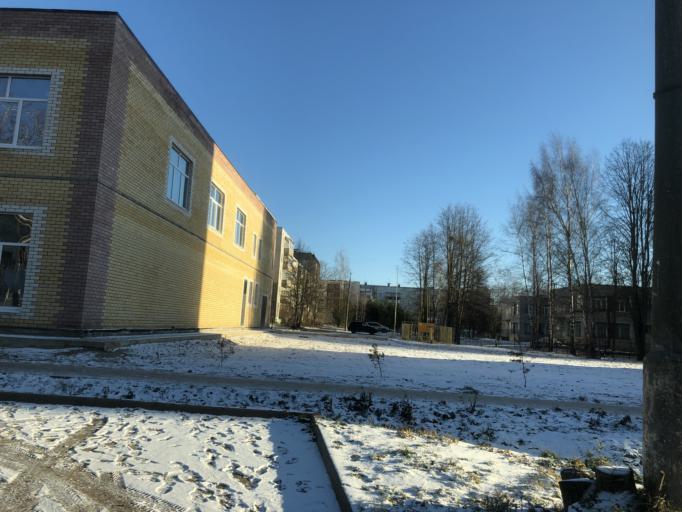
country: RU
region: Tverskaya
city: Rzhev
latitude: 56.2587
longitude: 34.3502
